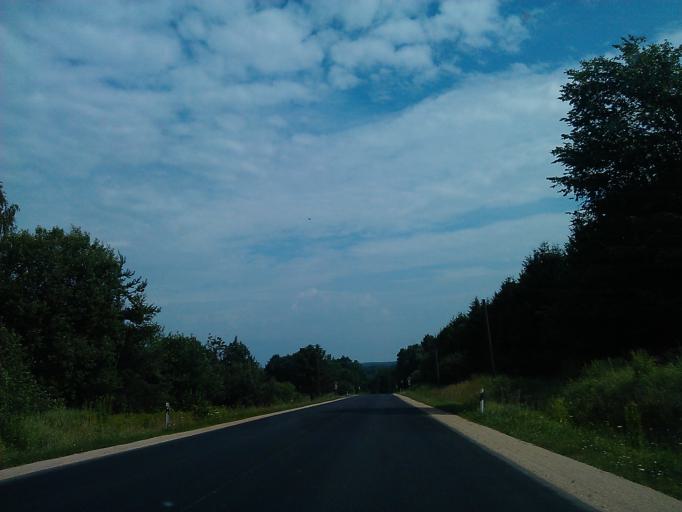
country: LV
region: Cesu Rajons
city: Cesis
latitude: 57.3312
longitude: 25.3172
